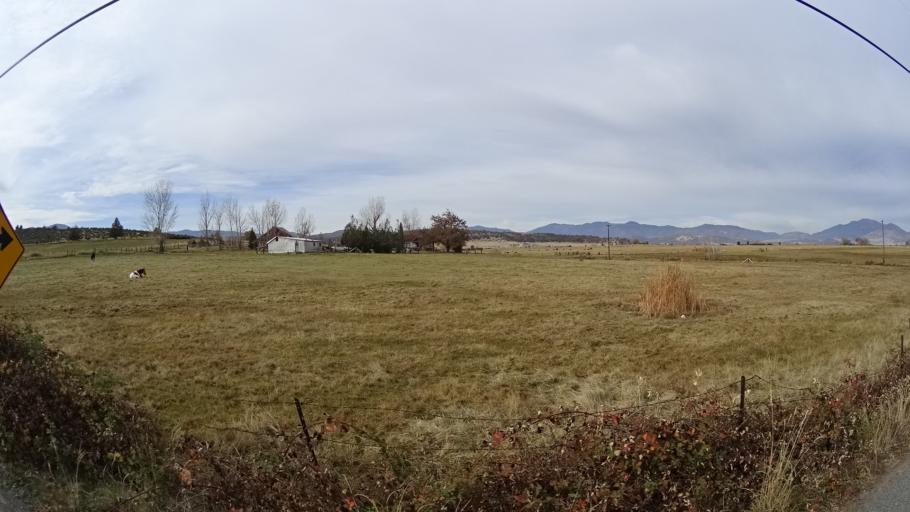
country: US
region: California
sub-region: Siskiyou County
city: Montague
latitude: 41.6992
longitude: -122.5495
